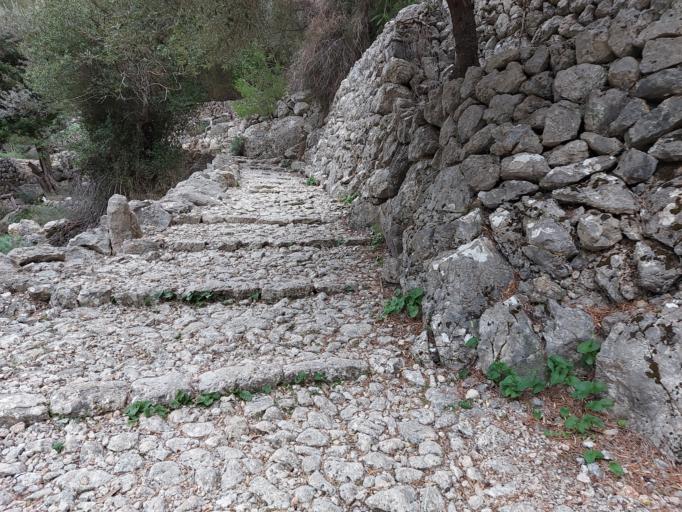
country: ES
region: Balearic Islands
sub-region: Illes Balears
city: Fornalutx
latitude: 39.7653
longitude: 2.7549
